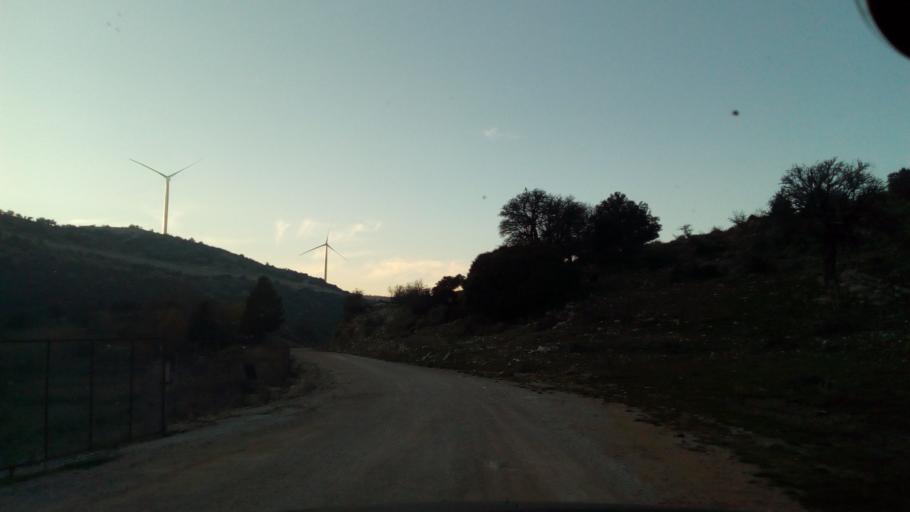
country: GR
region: West Greece
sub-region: Nomos Aitolias kai Akarnanias
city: Nafpaktos
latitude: 38.4607
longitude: 21.8352
